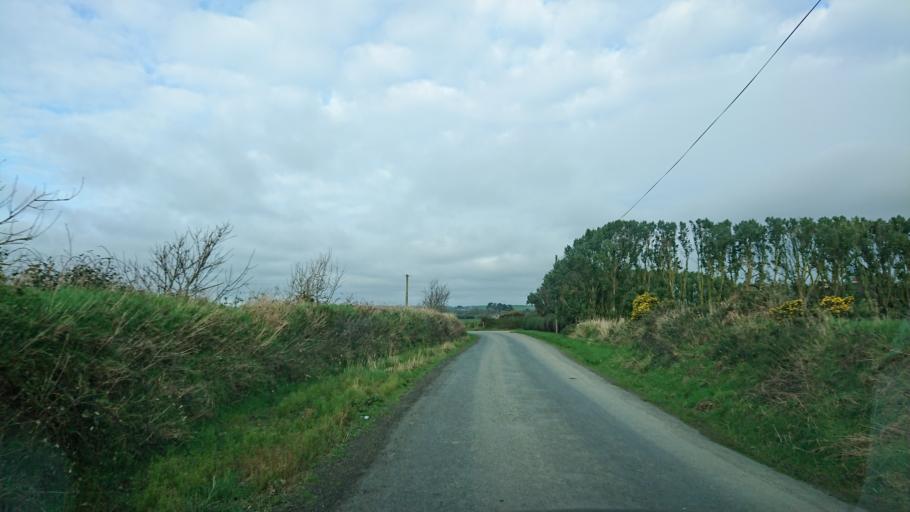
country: IE
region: Munster
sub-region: Waterford
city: Portlaw
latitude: 52.1440
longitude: -7.3052
